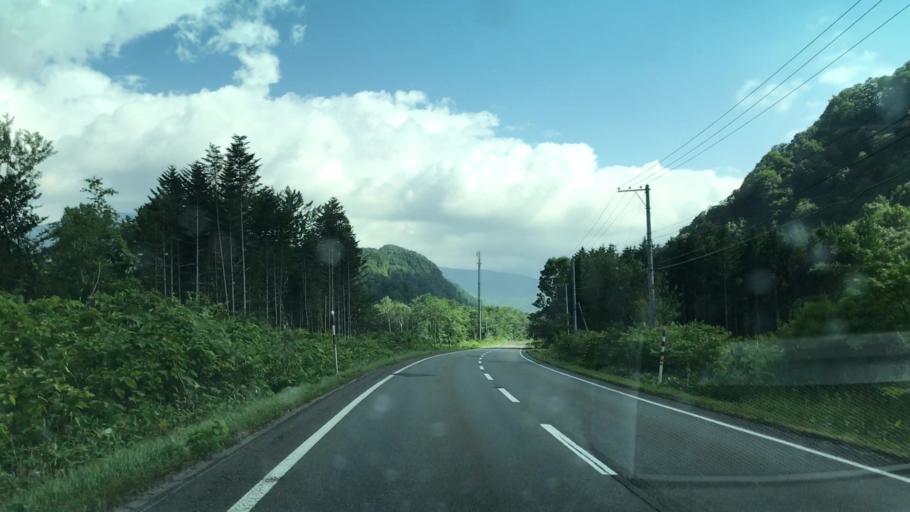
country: JP
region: Hokkaido
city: Shimo-furano
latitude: 42.8473
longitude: 142.4169
